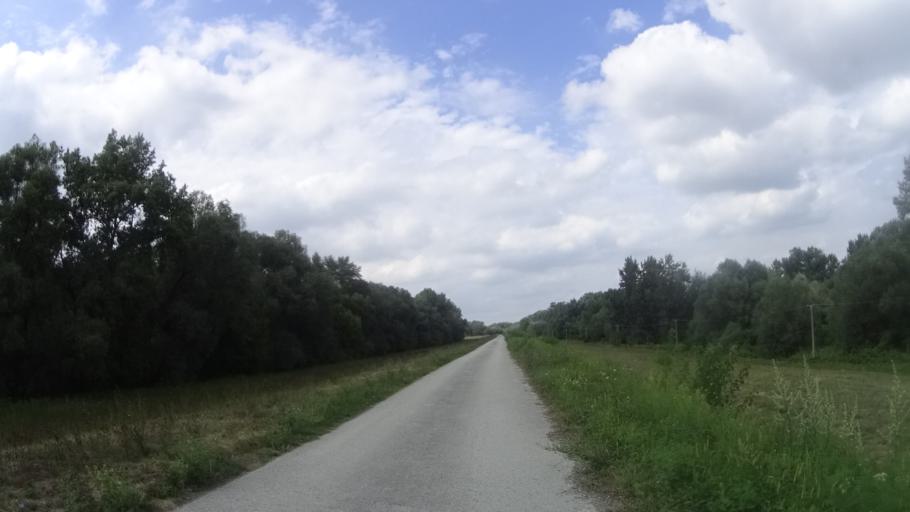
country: SK
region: Trnavsky
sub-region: Okres Dunajska Streda
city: Velky Meder
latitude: 47.7851
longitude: 17.6944
